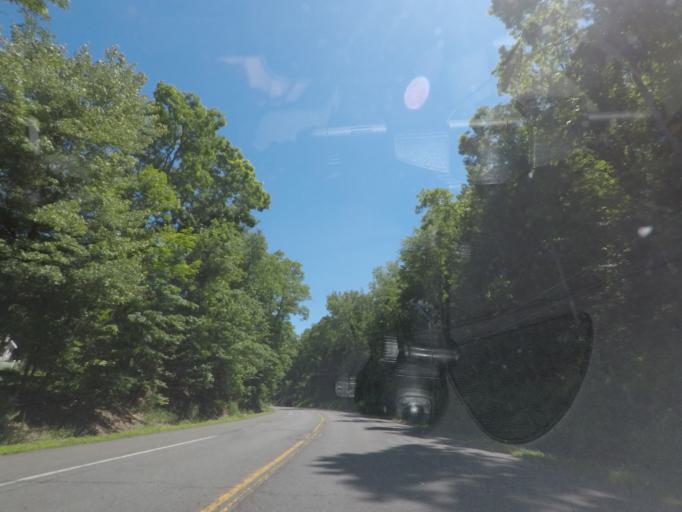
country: US
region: Massachusetts
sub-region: Hampden County
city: Westfield
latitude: 42.1635
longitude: -72.8314
